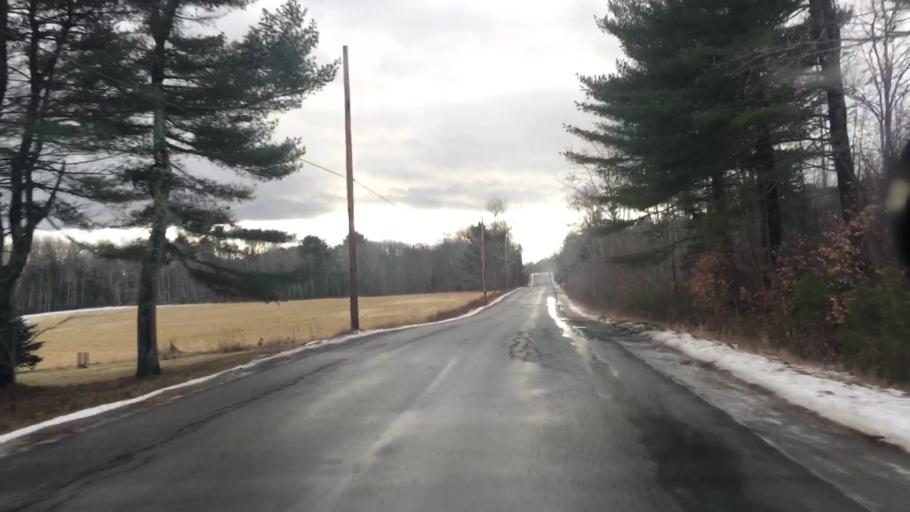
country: US
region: Maine
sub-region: Hancock County
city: Dedham
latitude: 44.6363
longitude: -68.7053
